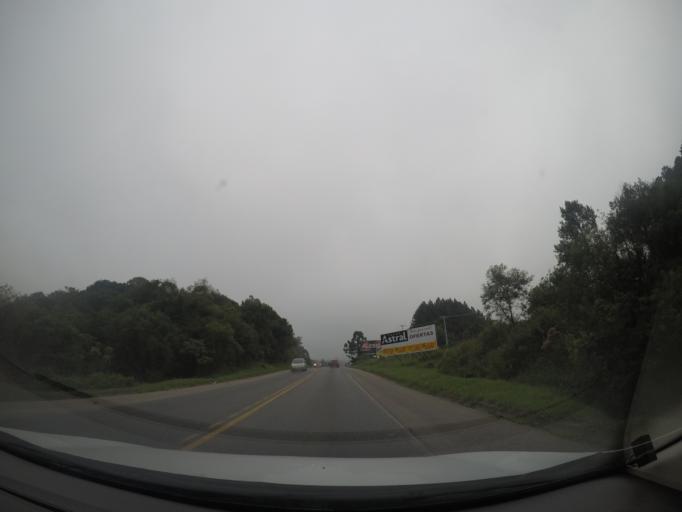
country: BR
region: Parana
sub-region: Almirante Tamandare
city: Almirante Tamandare
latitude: -25.3263
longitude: -49.2959
